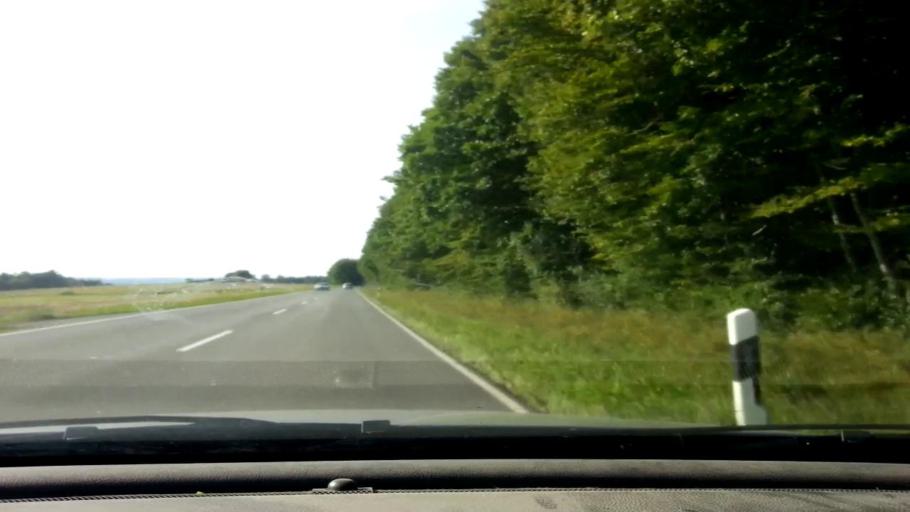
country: DE
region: Bavaria
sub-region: Upper Franconia
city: Zapfendorf
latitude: 50.0023
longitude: 10.9543
